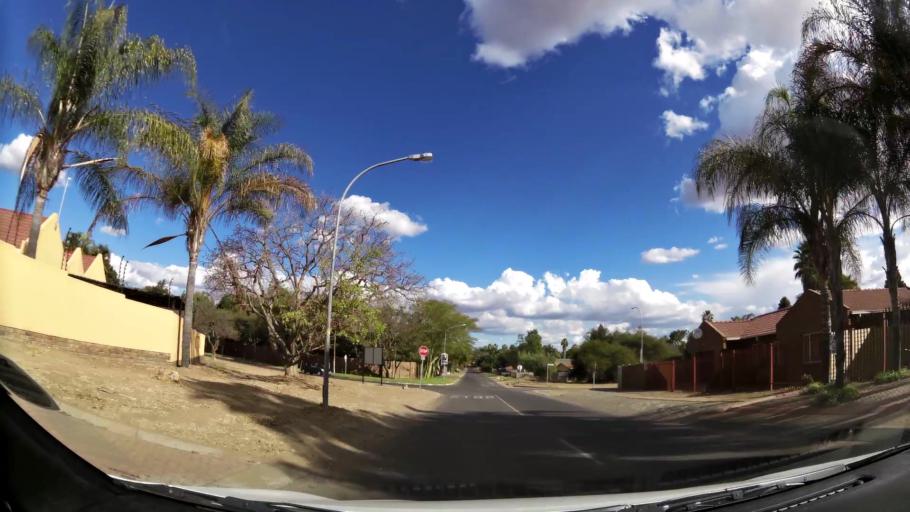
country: ZA
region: Limpopo
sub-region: Capricorn District Municipality
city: Polokwane
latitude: -23.8885
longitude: 29.4686
